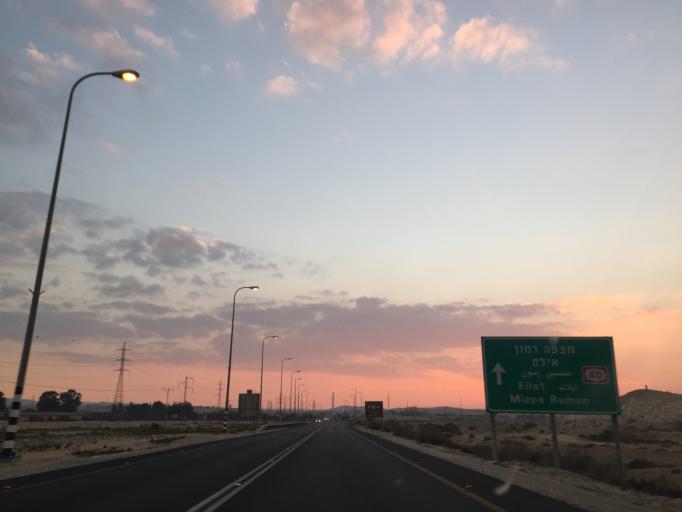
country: IL
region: Southern District
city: Yeroham
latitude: 31.0127
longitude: 34.7831
